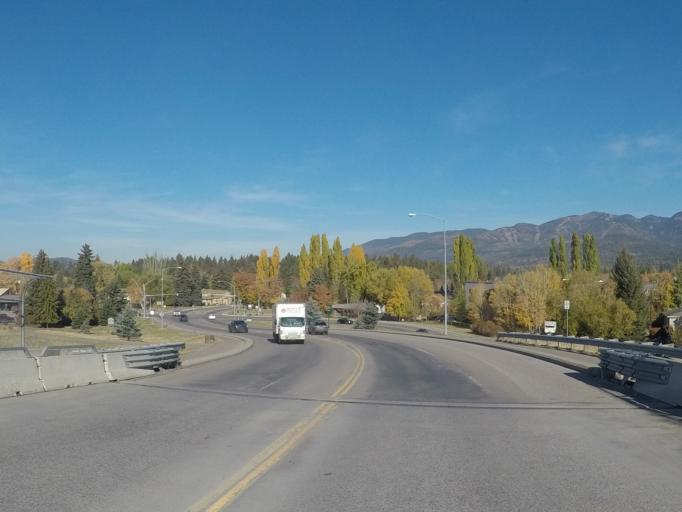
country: US
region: Montana
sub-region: Flathead County
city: Whitefish
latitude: 48.4146
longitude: -114.3390
